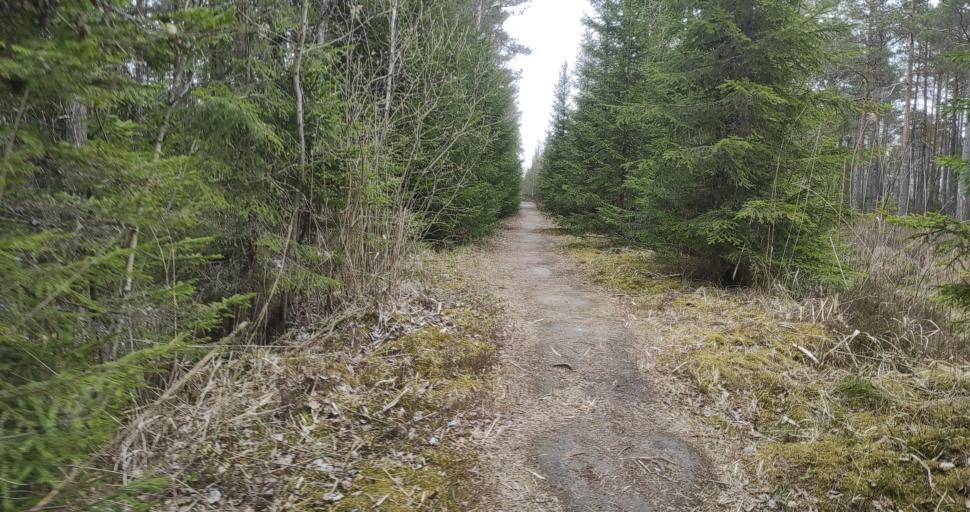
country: LV
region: Dundaga
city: Dundaga
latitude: 57.3454
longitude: 22.1497
